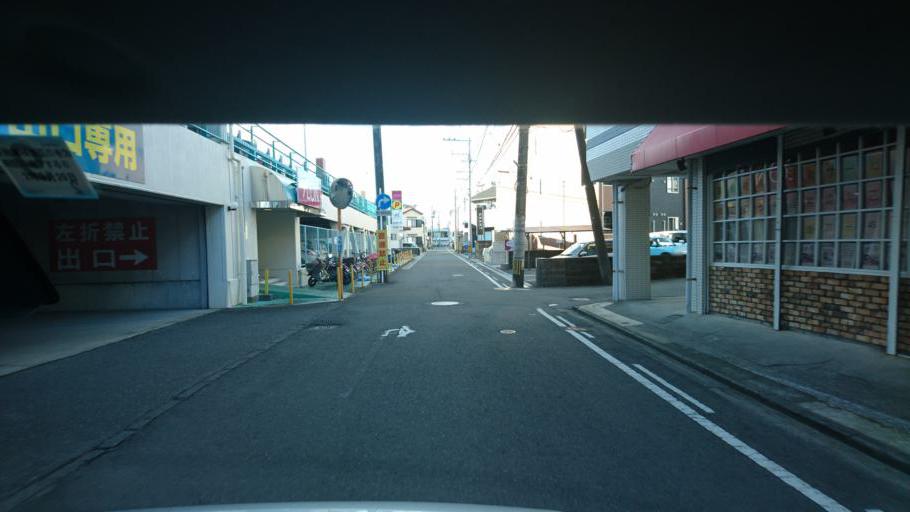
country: JP
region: Miyazaki
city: Miyazaki-shi
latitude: 31.8952
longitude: 131.4204
